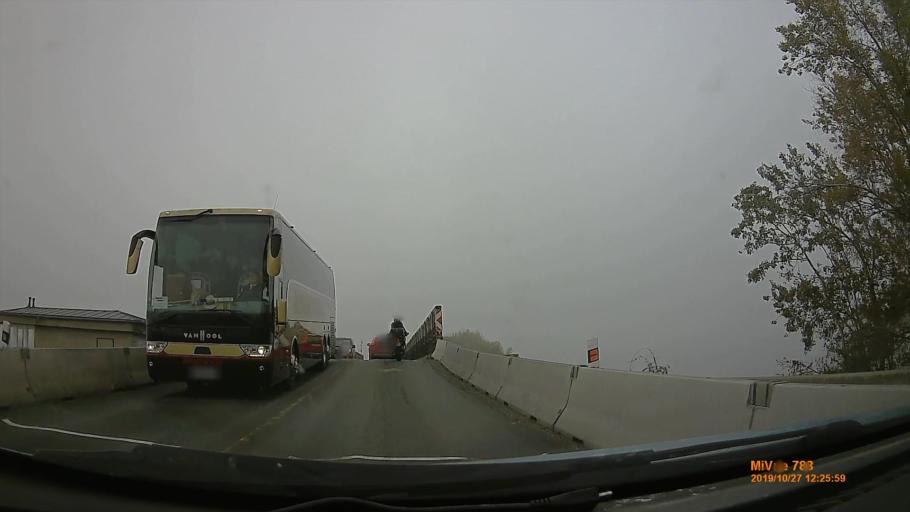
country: CZ
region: South Moravian
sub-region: Okres Breclav
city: Dolni Dunajovice
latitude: 48.8927
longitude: 16.5893
